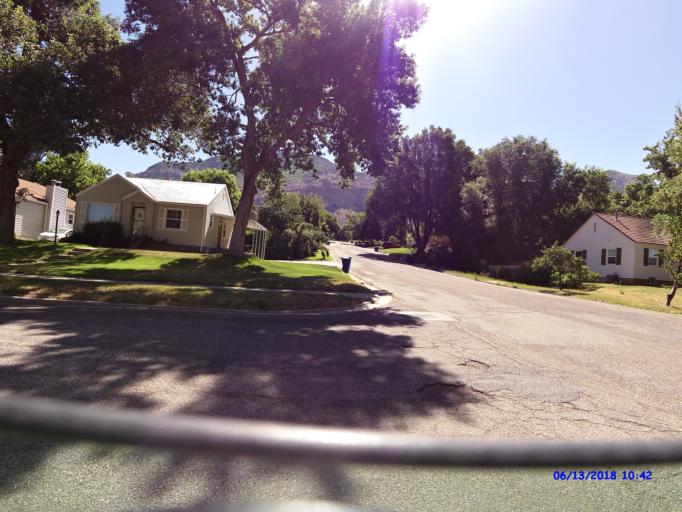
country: US
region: Utah
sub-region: Weber County
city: Ogden
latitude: 41.2235
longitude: -111.9403
